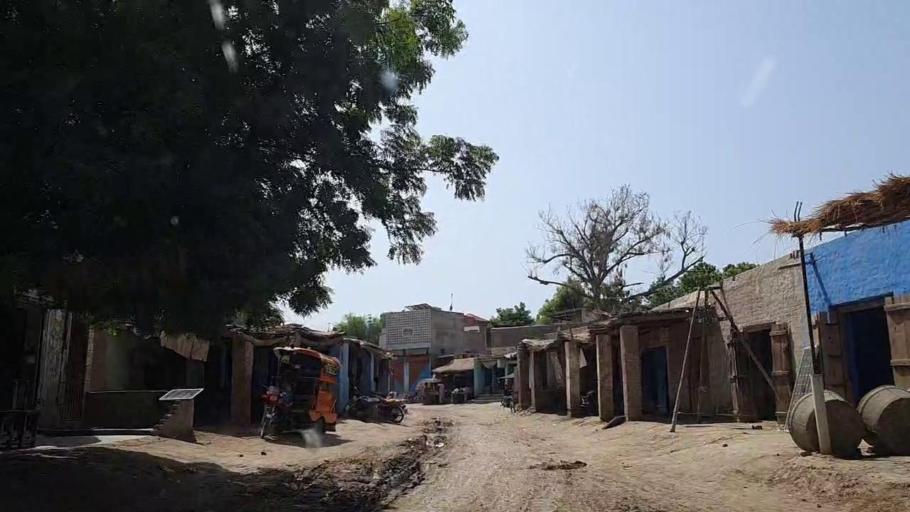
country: PK
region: Sindh
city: Naushahro Firoz
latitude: 26.8300
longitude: 68.0213
